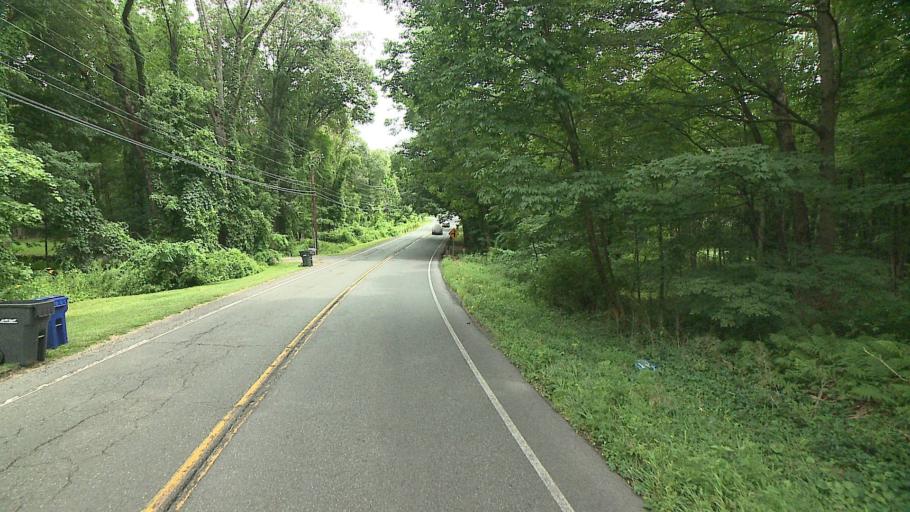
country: US
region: Connecticut
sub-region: Fairfield County
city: Newtown
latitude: 41.4733
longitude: -73.3620
